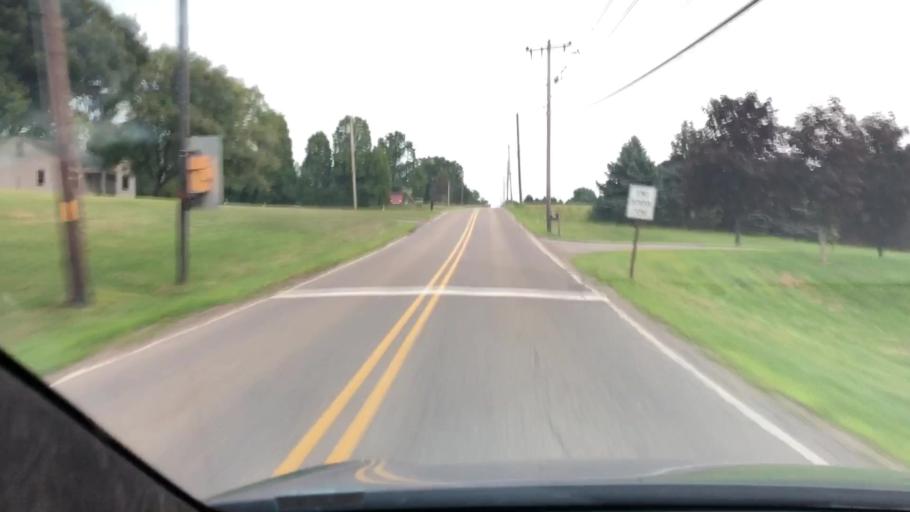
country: US
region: Pennsylvania
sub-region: Butler County
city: Shanor-Northvue
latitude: 40.9053
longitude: -79.9291
